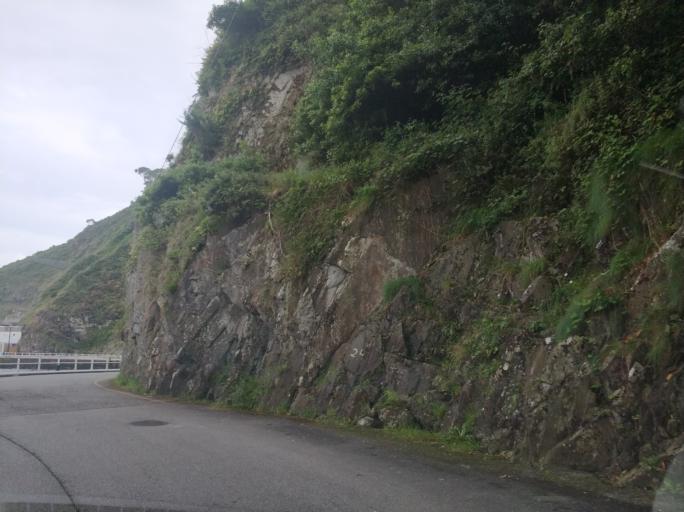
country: ES
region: Asturias
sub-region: Province of Asturias
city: Cudillero
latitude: 43.5635
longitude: -6.1472
